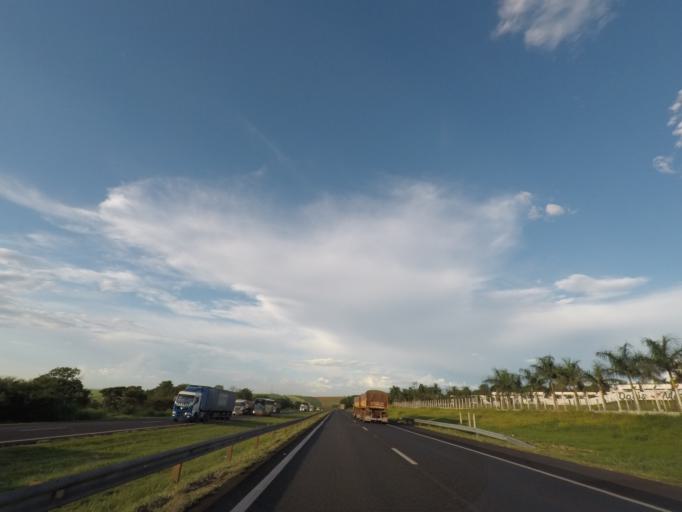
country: BR
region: Sao Paulo
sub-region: Ituverava
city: Ituverava
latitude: -20.2955
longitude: -47.7987
